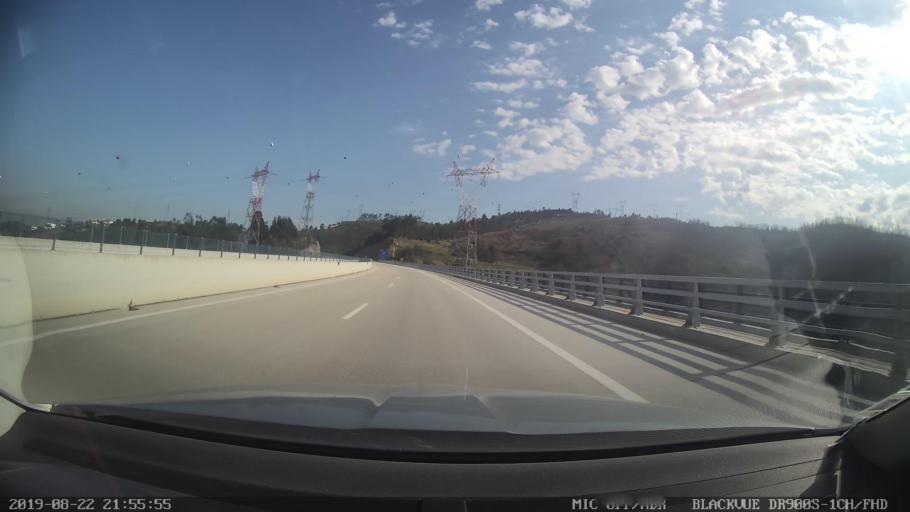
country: PT
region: Coimbra
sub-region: Coimbra
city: Coimbra
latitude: 40.1615
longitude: -8.3782
